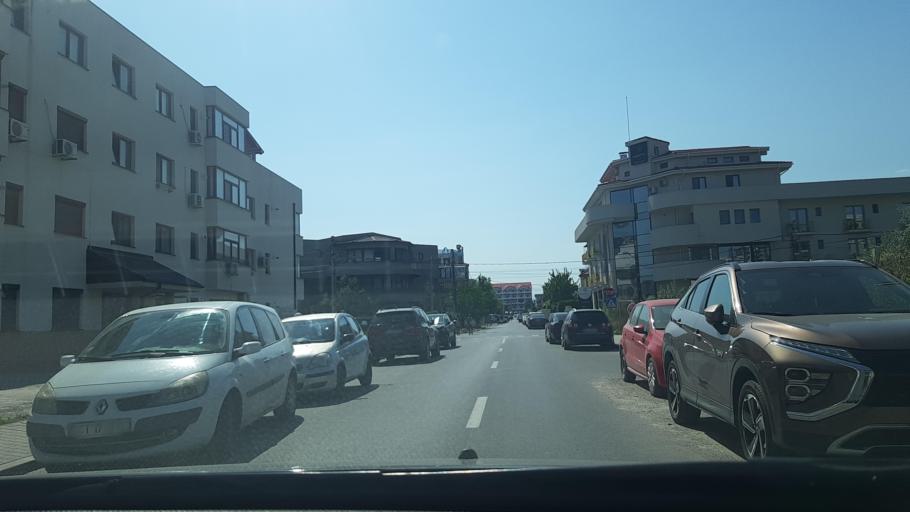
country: RO
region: Constanta
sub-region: Comuna Navodari
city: Navodari
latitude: 44.3050
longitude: 28.6256
